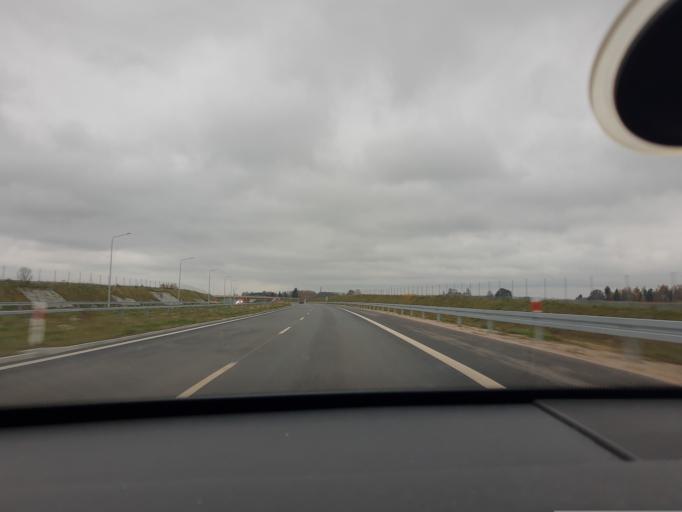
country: PL
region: Lodz Voivodeship
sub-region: Powiat pabianicki
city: Pabianice
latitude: 51.7061
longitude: 19.3419
